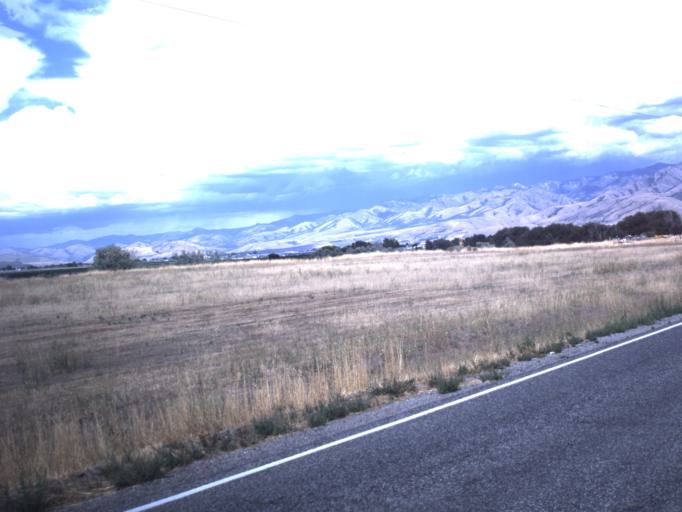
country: US
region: Utah
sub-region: Cache County
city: Lewiston
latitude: 41.9146
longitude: -111.9181
